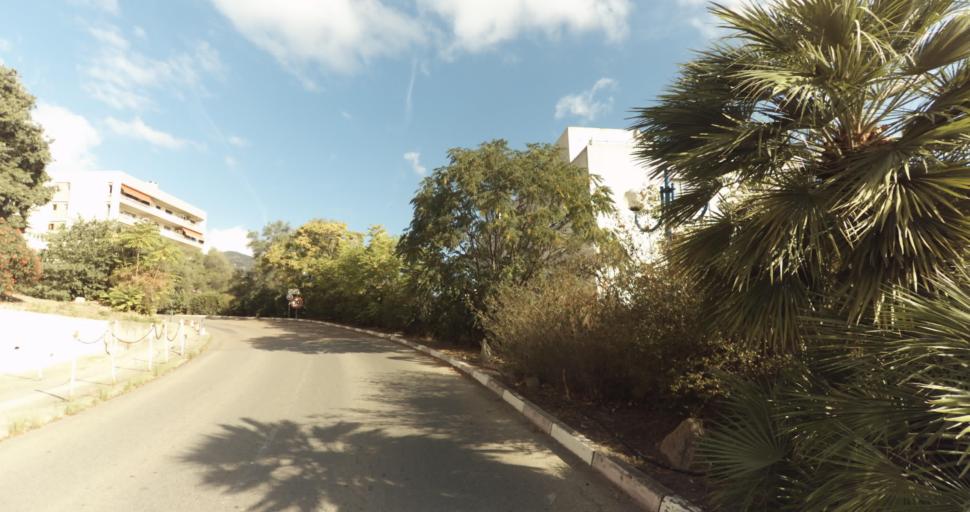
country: FR
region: Corsica
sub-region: Departement de la Corse-du-Sud
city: Ajaccio
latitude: 41.9233
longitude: 8.7352
